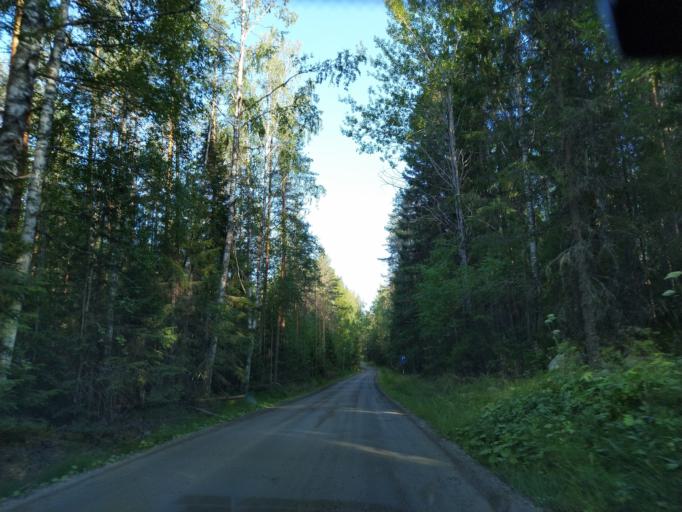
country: FI
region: Central Finland
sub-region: Jaemsae
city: Kuhmoinen
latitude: 61.6783
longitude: 24.9887
